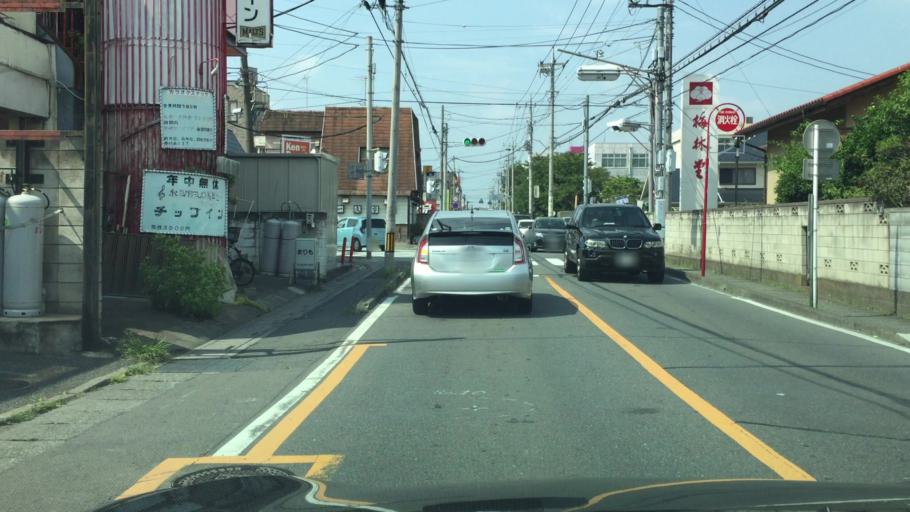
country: JP
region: Saitama
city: Yono
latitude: 35.9191
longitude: 139.6085
